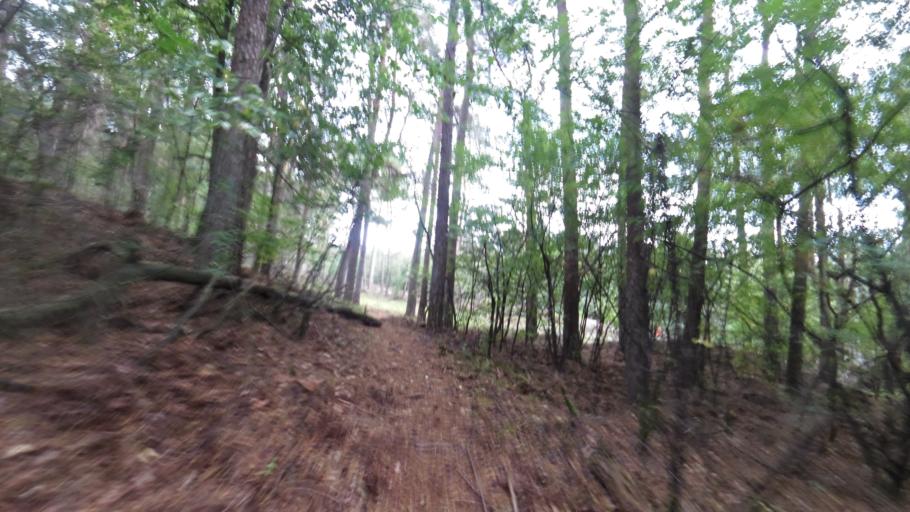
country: NL
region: Gelderland
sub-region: Gemeente Barneveld
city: Stroe
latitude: 52.1702
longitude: 5.7333
